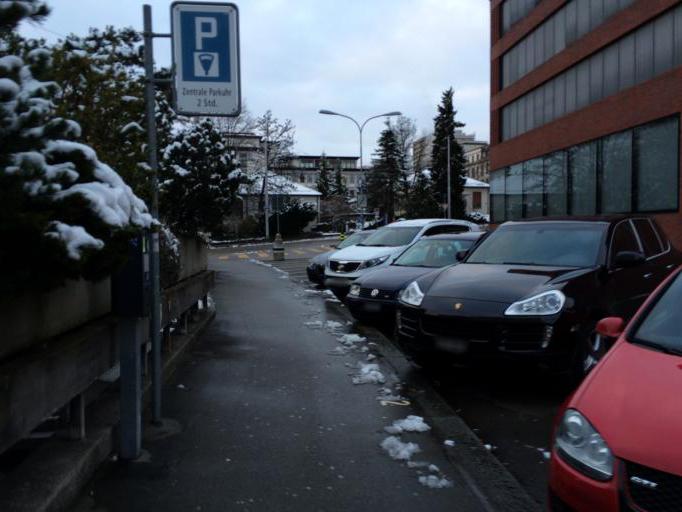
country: CH
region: Zurich
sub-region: Bezirk Zuerich
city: Zurich
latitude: 47.3749
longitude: 8.5533
